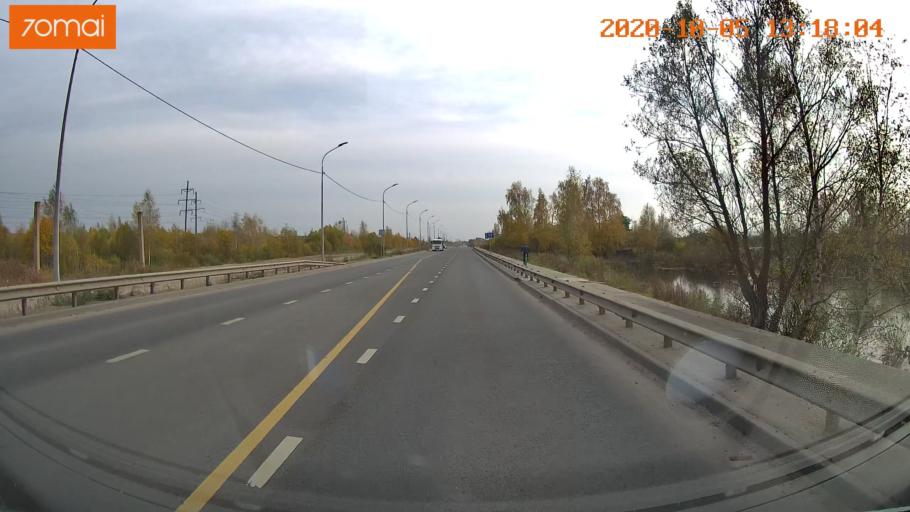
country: RU
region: Ivanovo
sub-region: Gorod Ivanovo
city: Ivanovo
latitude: 56.9806
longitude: 40.9163
